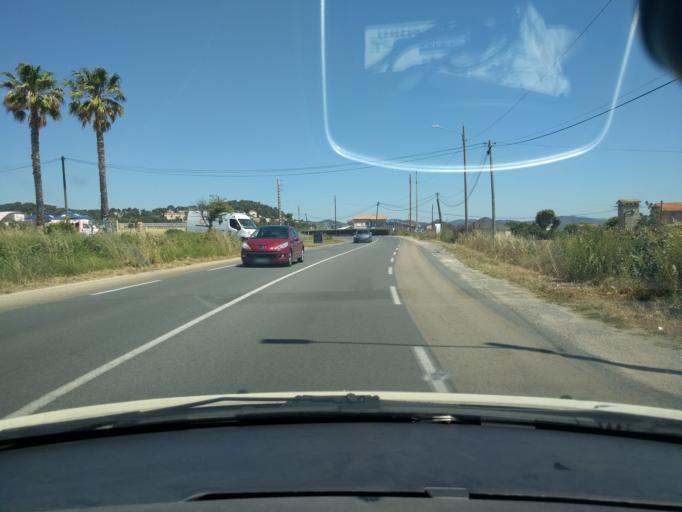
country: FR
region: Provence-Alpes-Cote d'Azur
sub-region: Departement du Var
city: Hyeres
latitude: 43.0850
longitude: 6.1288
